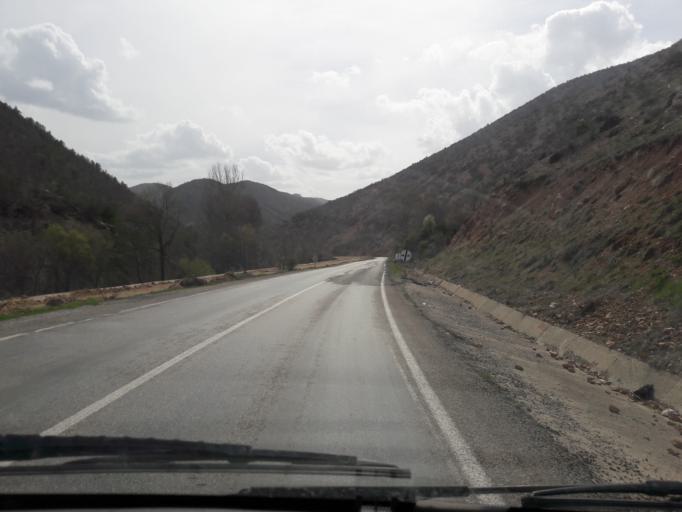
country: TR
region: Gumushane
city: Kale
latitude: 40.3930
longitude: 39.5869
